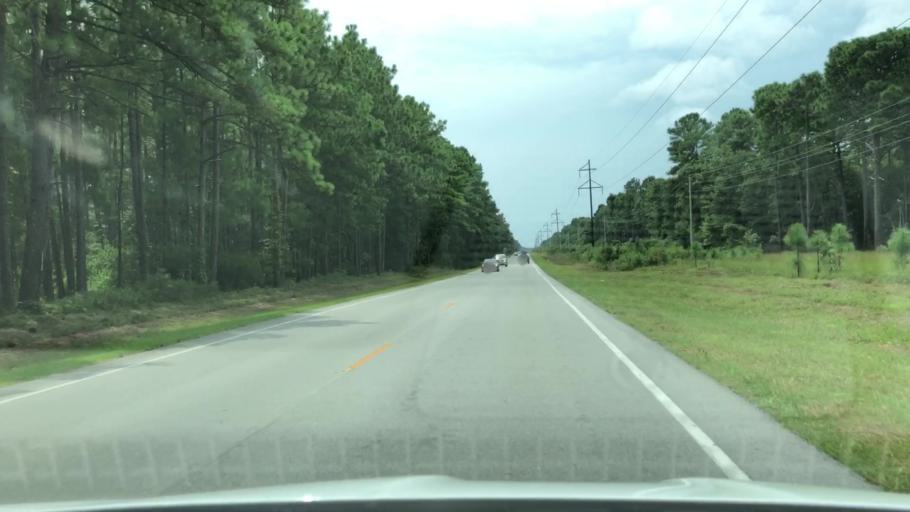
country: US
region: North Carolina
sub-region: Carteret County
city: Newport
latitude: 34.7610
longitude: -76.8712
